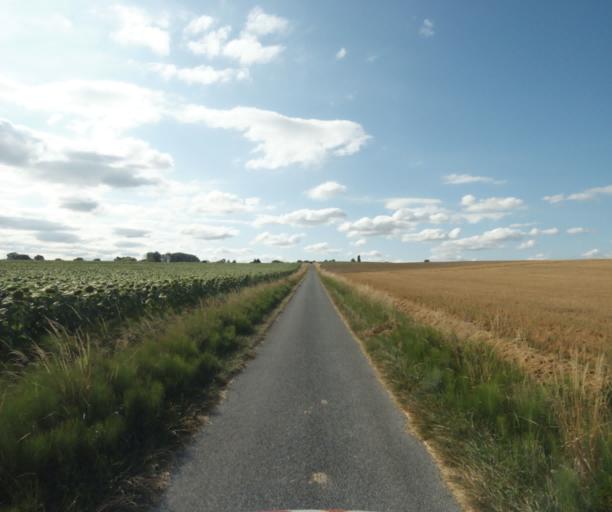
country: FR
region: Midi-Pyrenees
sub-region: Departement du Tarn
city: Puylaurens
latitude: 43.5266
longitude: 1.9968
